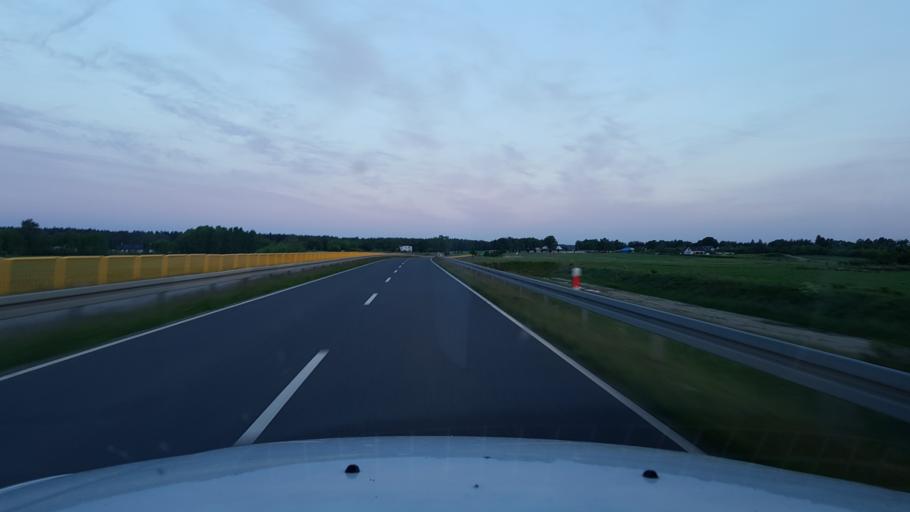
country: PL
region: West Pomeranian Voivodeship
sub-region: Powiat goleniowski
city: Goleniow
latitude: 53.5722
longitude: 14.8705
